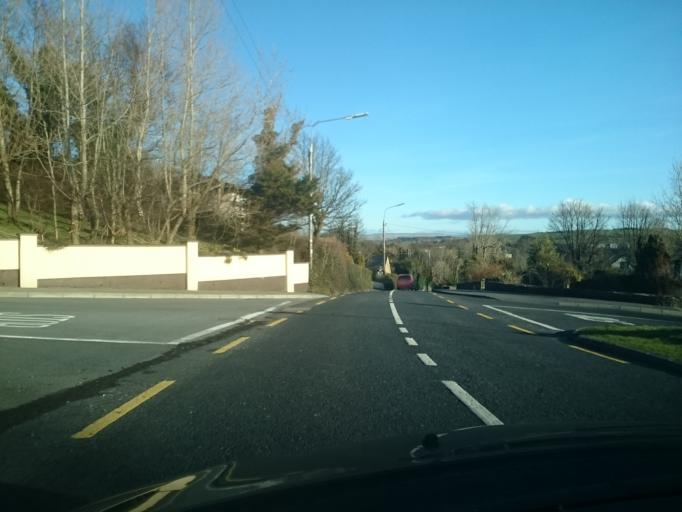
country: IE
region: Connaught
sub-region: Maigh Eo
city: Westport
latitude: 53.8048
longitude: -9.5222
